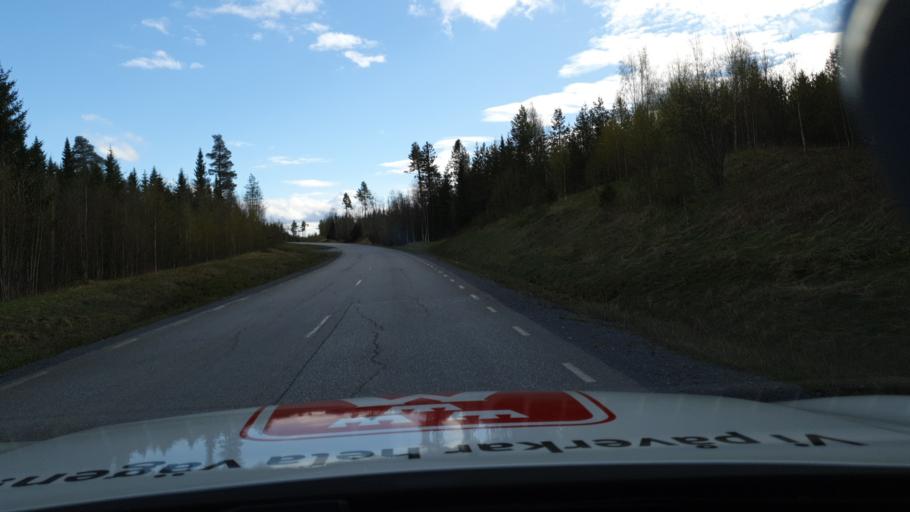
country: SE
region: Jaemtland
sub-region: Krokoms Kommun
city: Krokom
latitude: 63.2724
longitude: 14.4384
